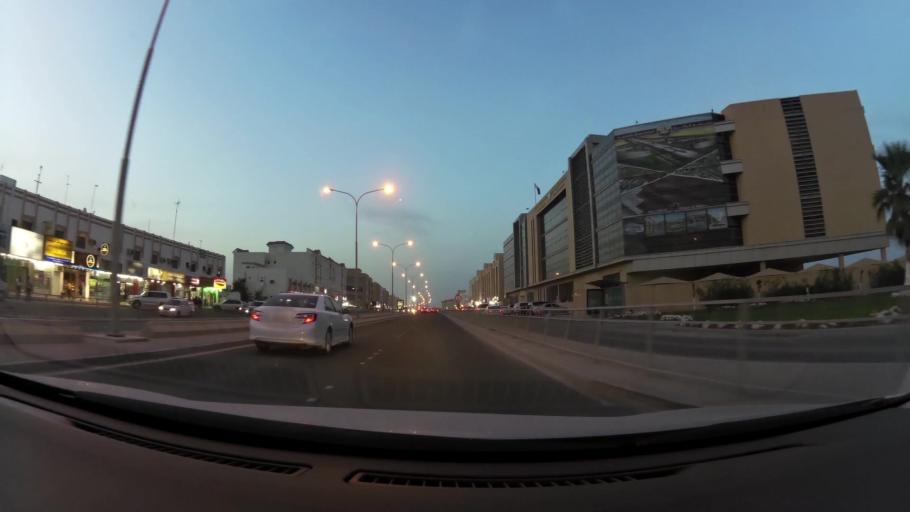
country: QA
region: Al Wakrah
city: Al Wakrah
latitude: 25.1664
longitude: 51.5978
